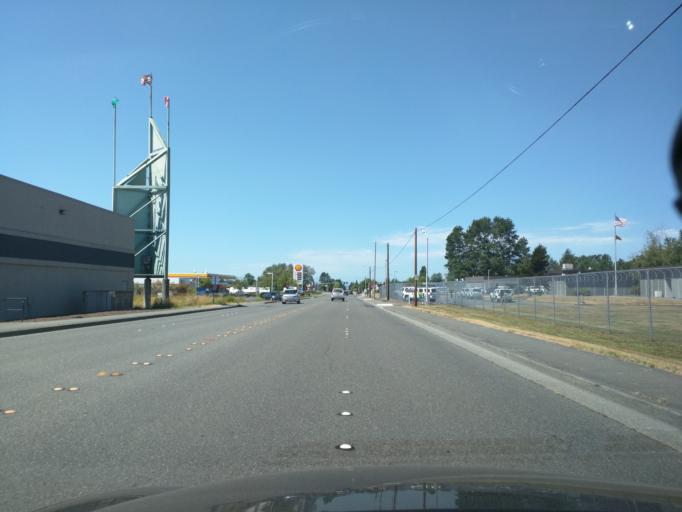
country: US
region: Washington
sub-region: Whatcom County
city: Blaine
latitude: 48.9940
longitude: -122.7300
